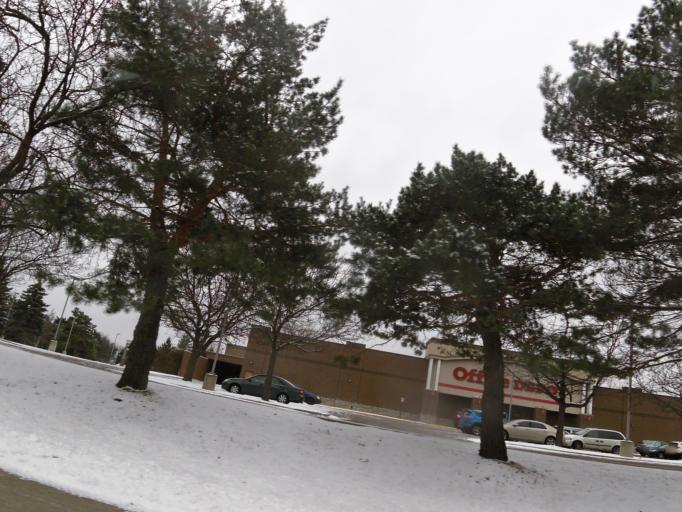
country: US
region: Minnesota
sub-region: Hennepin County
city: Eden Prairie
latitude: 44.8598
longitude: -93.4241
